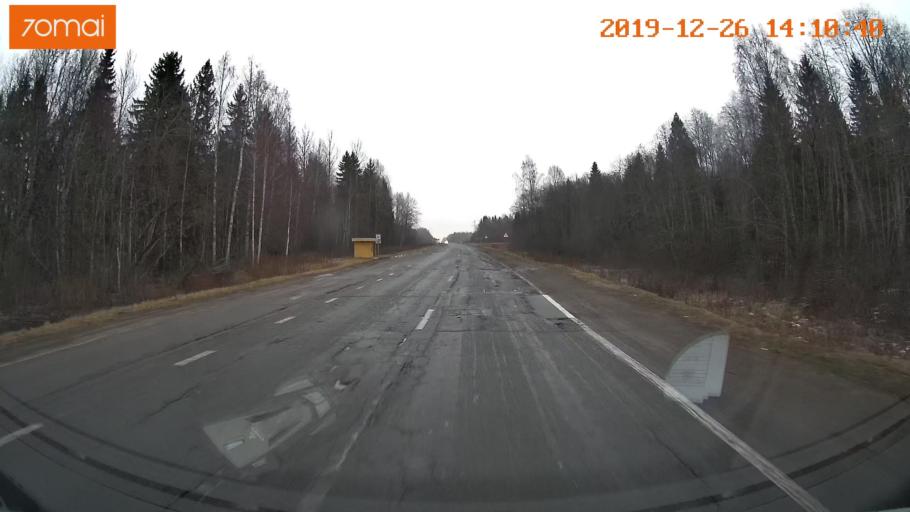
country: RU
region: Jaroslavl
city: Poshekhon'ye
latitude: 58.5085
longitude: 38.9582
